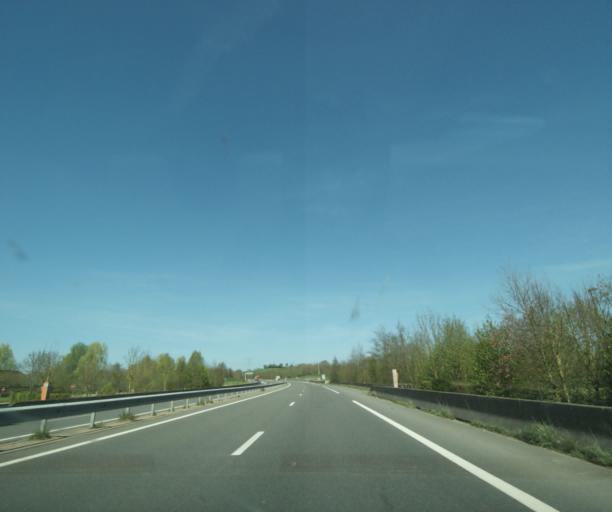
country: FR
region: Bourgogne
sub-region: Departement de la Nievre
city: Pougues-les-Eaux
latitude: 47.0739
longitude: 3.1273
